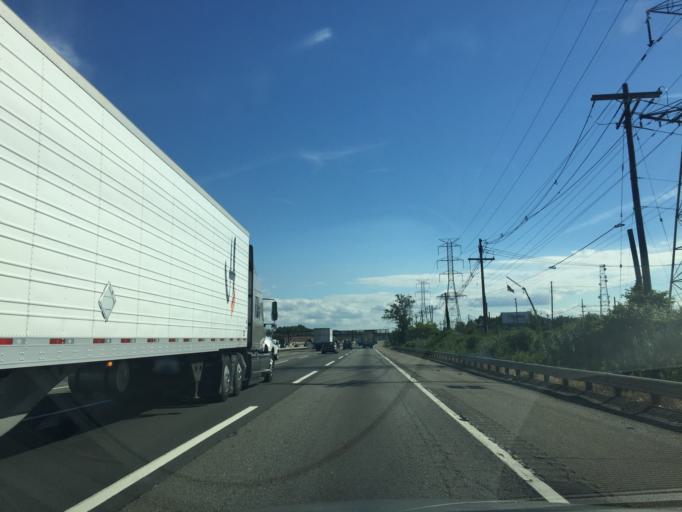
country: US
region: New Jersey
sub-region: Middlesex County
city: Carteret
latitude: 40.5888
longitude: -74.2386
